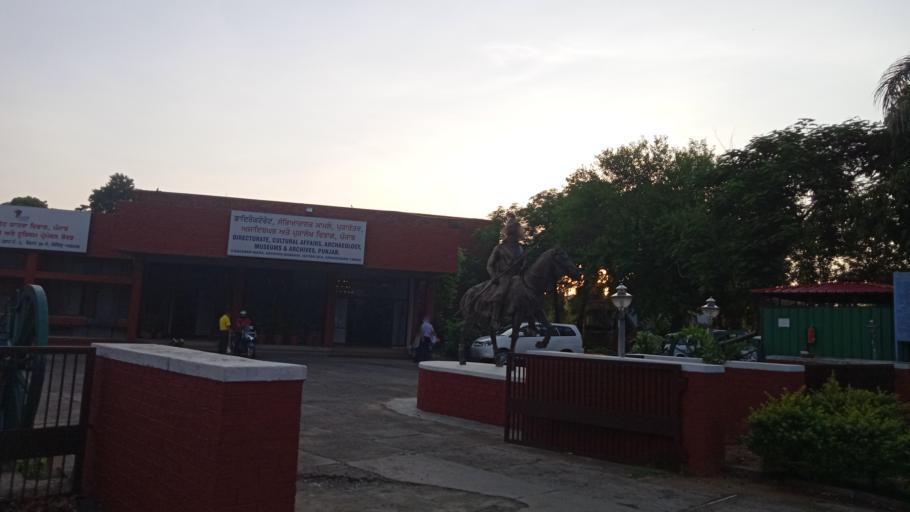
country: IN
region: Chandigarh
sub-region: Chandigarh
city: Chandigarh
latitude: 30.7486
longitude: 76.7508
